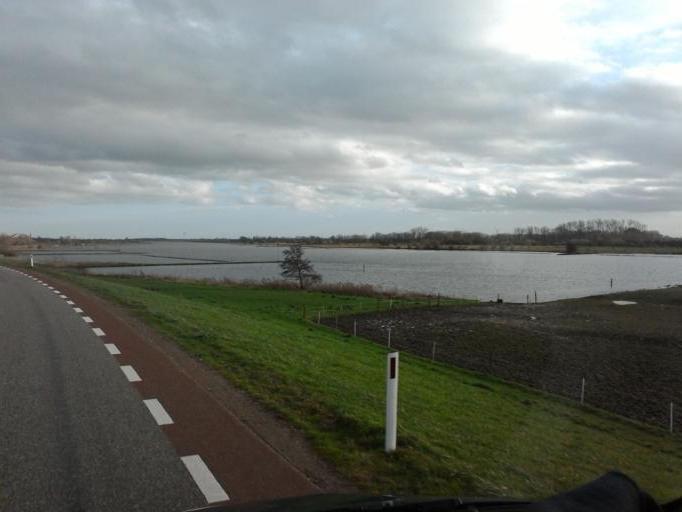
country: NL
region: Utrecht
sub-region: Gemeente Houten
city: Houten
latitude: 51.9714
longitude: 5.1715
